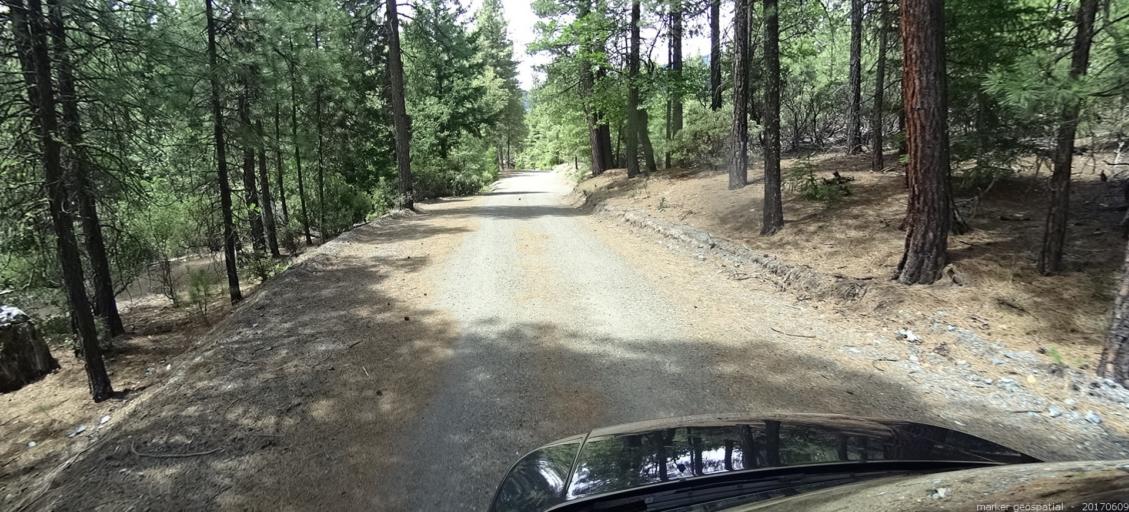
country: US
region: California
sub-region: Siskiyou County
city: Yreka
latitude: 41.3647
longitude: -122.8909
